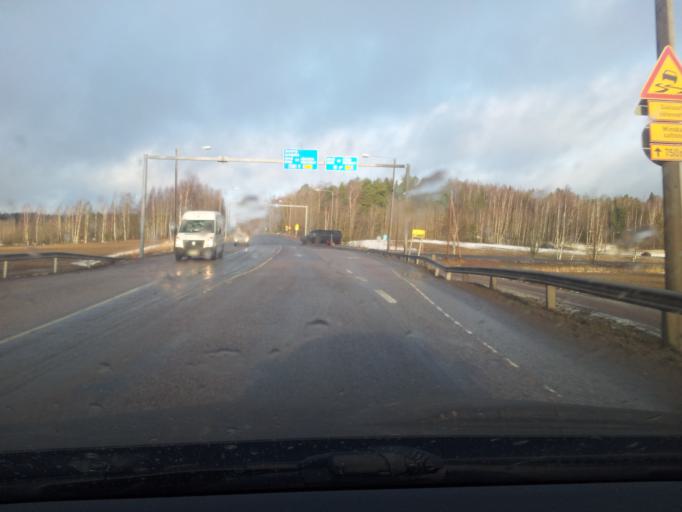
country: FI
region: Uusimaa
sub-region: Helsinki
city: Espoo
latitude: 60.1883
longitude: 24.5826
